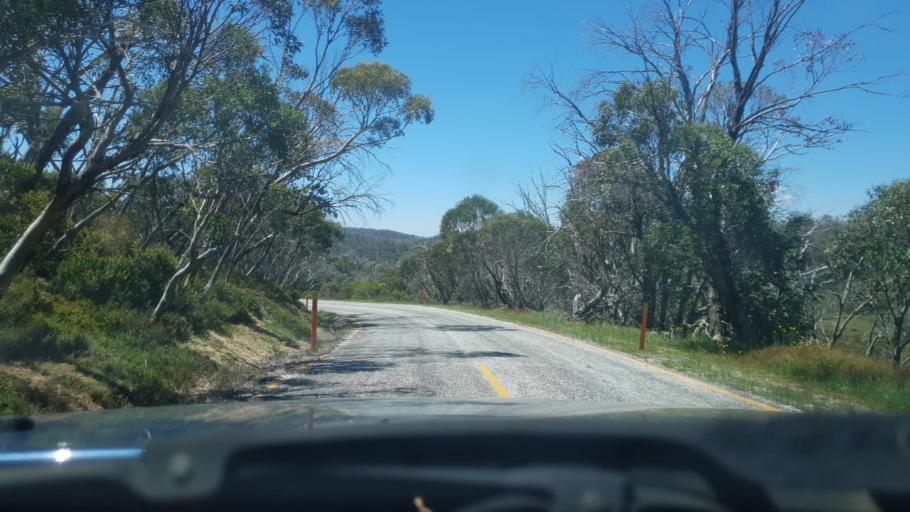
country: AU
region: Victoria
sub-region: Alpine
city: Mount Beauty
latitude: -36.9268
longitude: 147.3000
